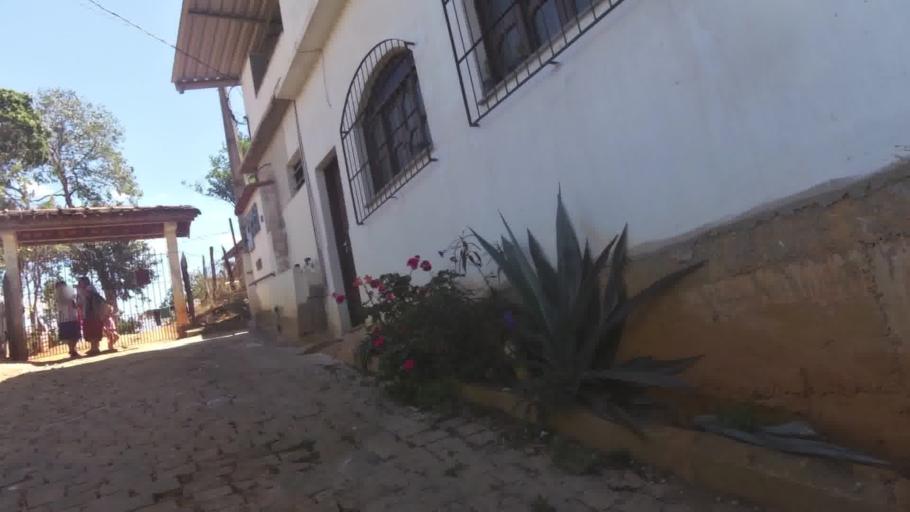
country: BR
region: Espirito Santo
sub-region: Cachoeiro De Itapemirim
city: Cachoeiro de Itapemirim
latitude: -20.9196
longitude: -41.1847
